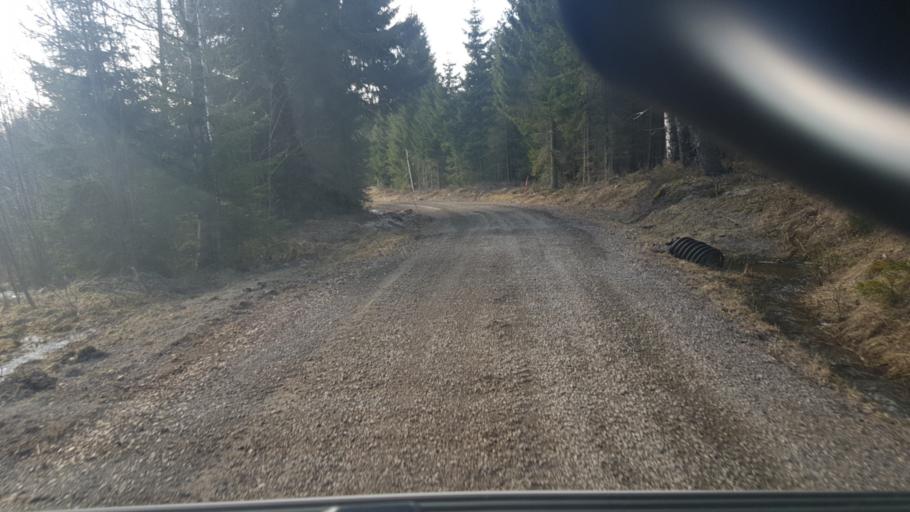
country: SE
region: Vaermland
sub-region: Eda Kommun
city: Amotfors
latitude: 59.8340
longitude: 12.3730
